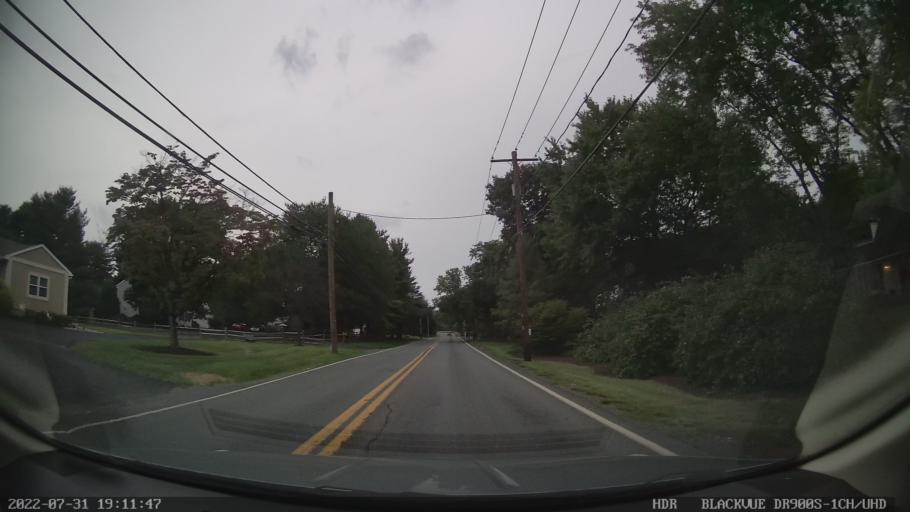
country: US
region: Pennsylvania
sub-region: Lehigh County
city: Fountain Hill
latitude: 40.5754
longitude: -75.3794
